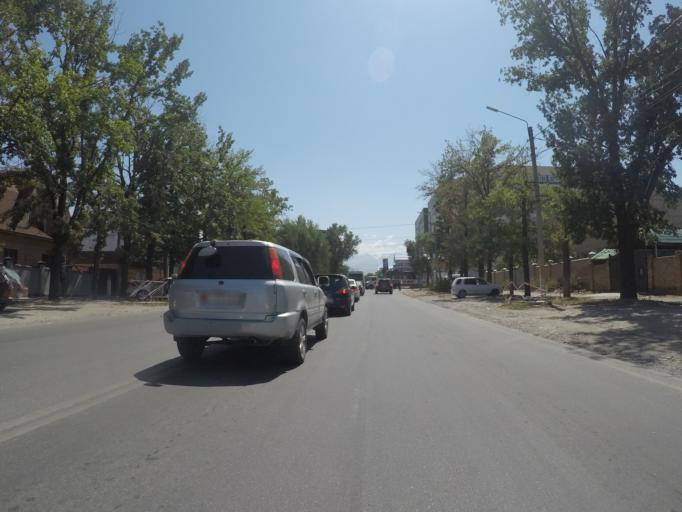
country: KG
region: Chuy
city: Bishkek
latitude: 42.8443
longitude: 74.5769
